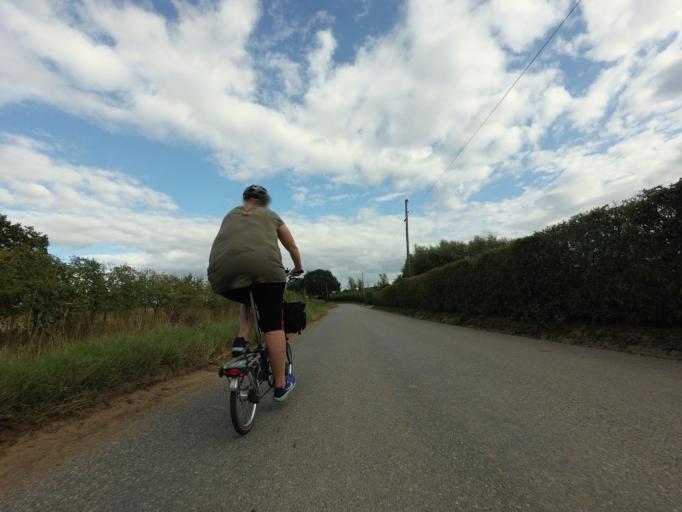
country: GB
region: England
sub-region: Kent
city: Marden
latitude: 51.2113
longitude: 0.4988
